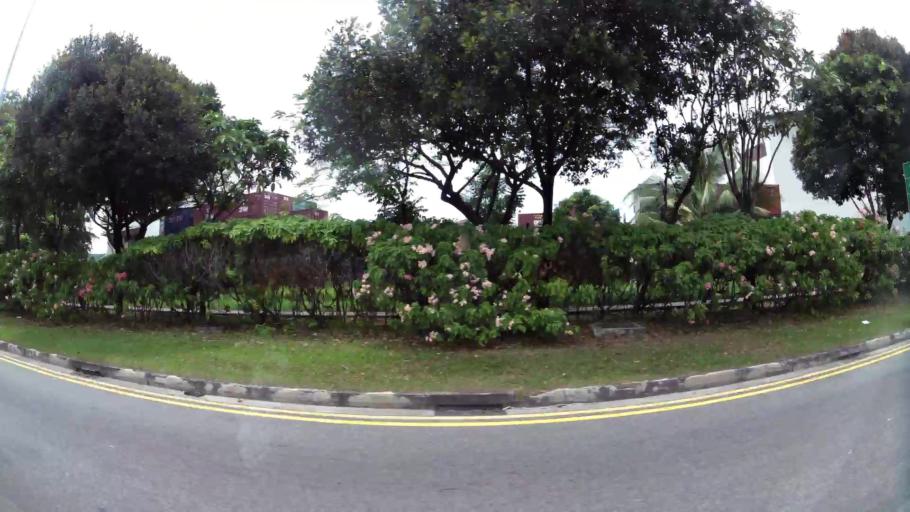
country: SG
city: Singapore
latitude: 1.3180
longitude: 103.6961
